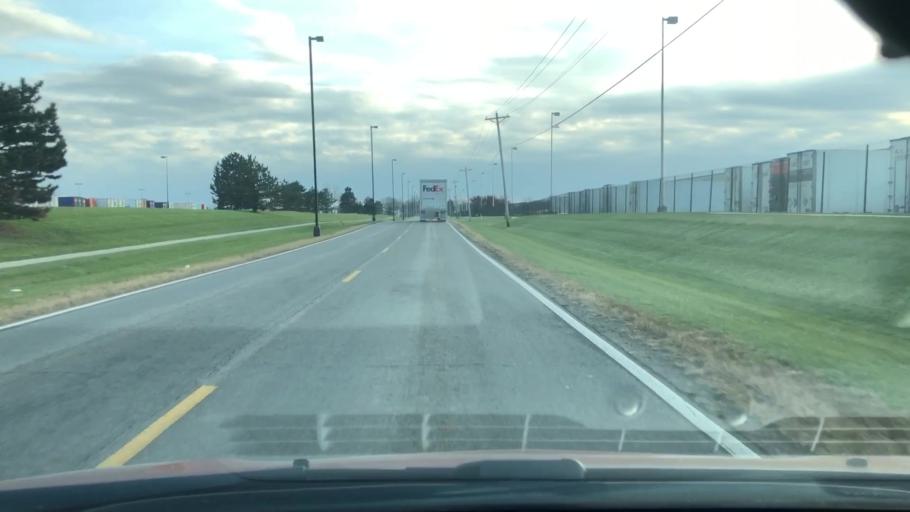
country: US
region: Ohio
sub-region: Franklin County
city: Obetz
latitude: 39.8357
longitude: -82.9442
